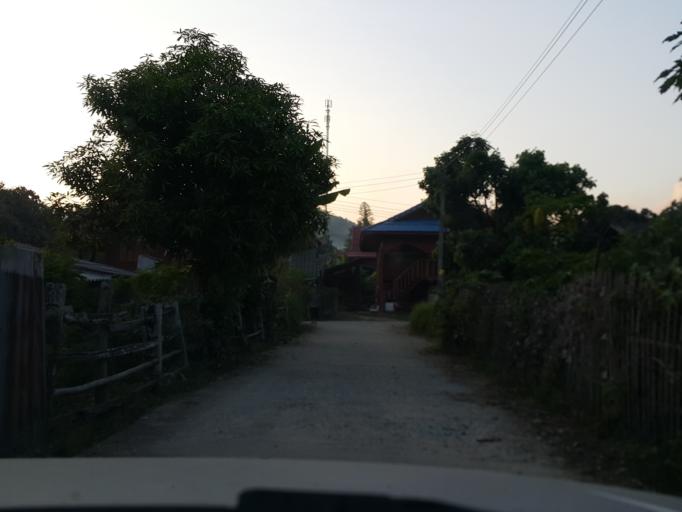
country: TH
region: Lamphun
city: Ban Thi
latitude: 18.5985
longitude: 99.2719
